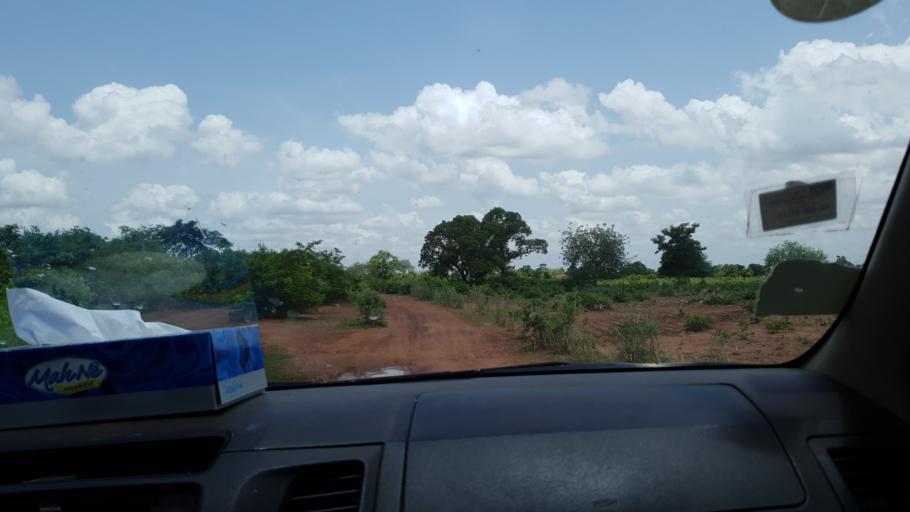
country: ML
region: Koulikoro
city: Banamba
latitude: 13.3784
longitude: -7.2130
